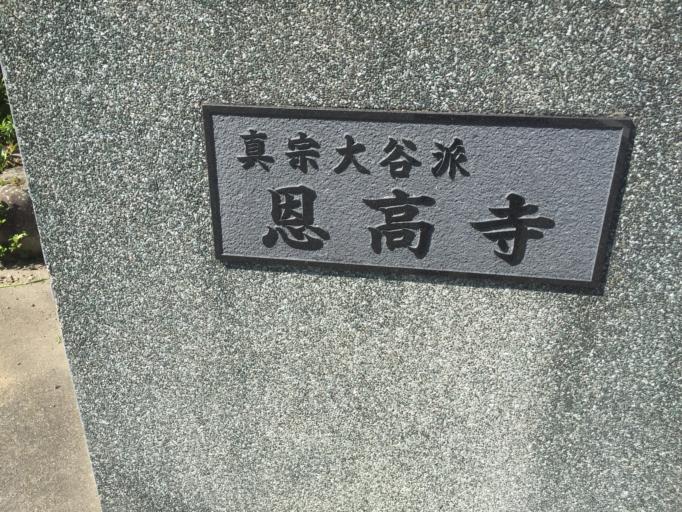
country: JP
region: Shizuoka
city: Fukuroi
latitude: 34.6800
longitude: 137.9770
